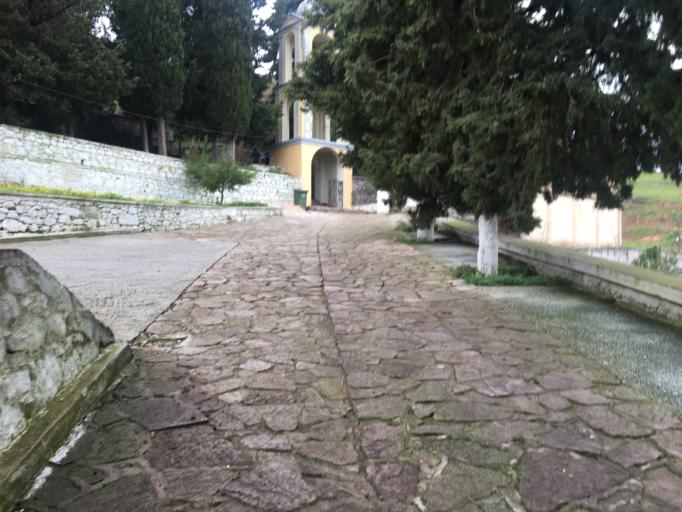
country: GR
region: North Aegean
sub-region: Nomos Lesvou
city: Agia Paraskevi
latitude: 39.2504
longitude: 26.2681
